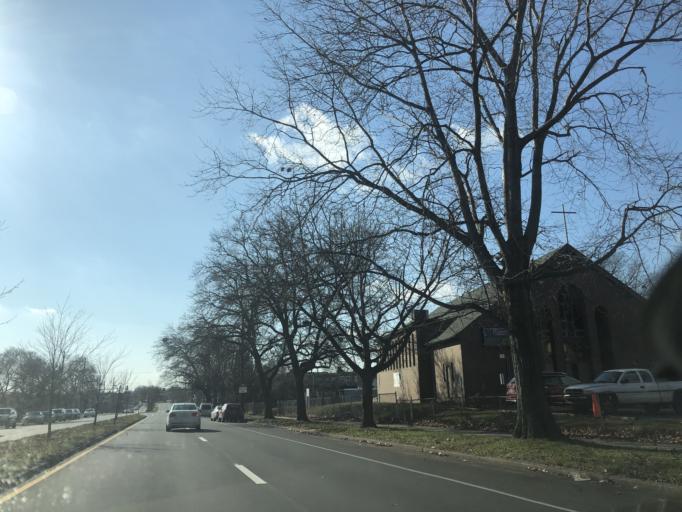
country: US
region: Pennsylvania
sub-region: Delaware County
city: Colwyn
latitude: 39.9224
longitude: -75.2233
